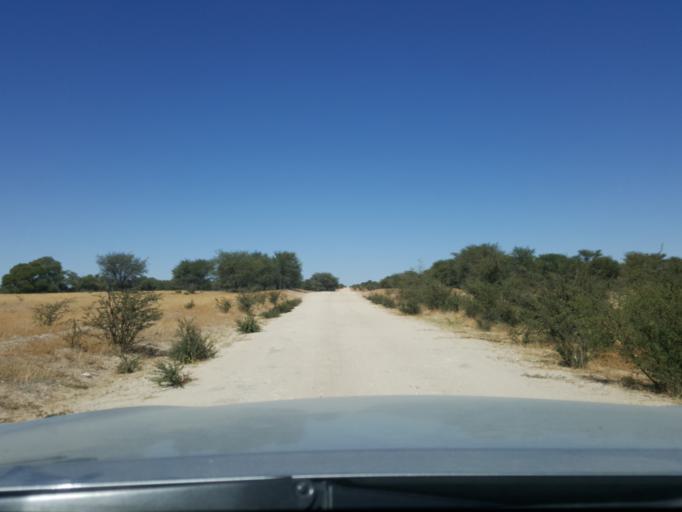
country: BW
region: Kgalagadi
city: Hukuntsi
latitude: -23.9825
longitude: 21.2086
